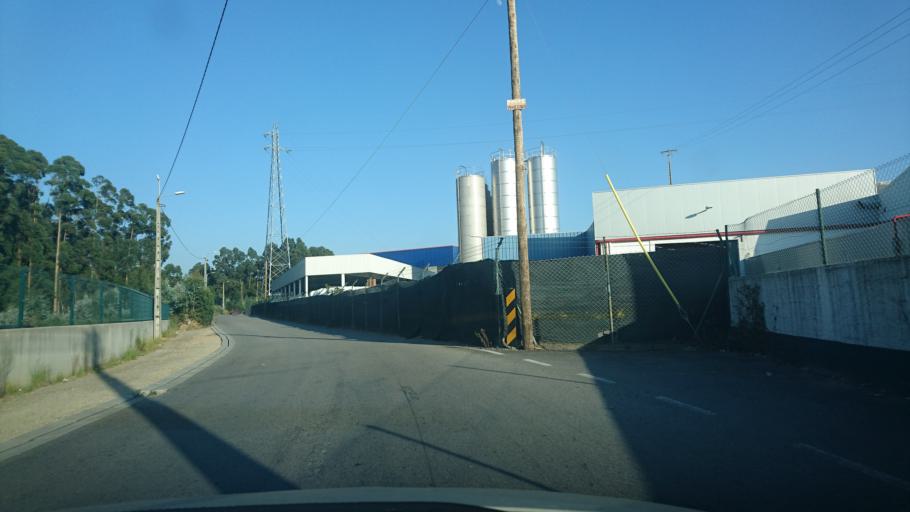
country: PT
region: Aveiro
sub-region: Ovar
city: Esmoriz
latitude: 40.9656
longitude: -8.6131
